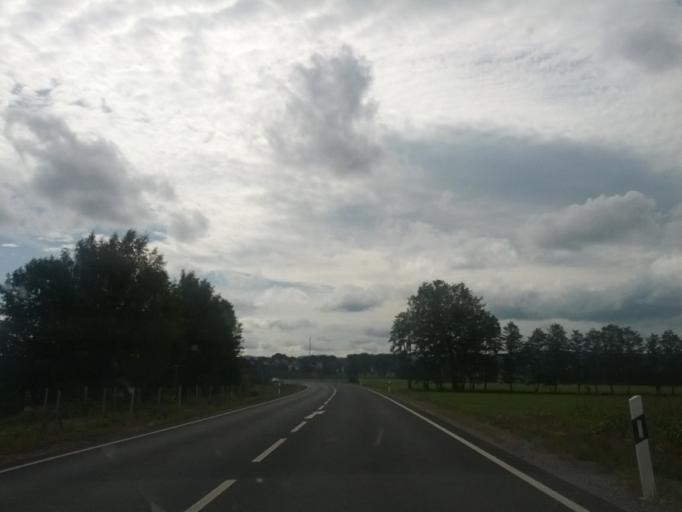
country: DE
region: Thuringia
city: Barchfeld
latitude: 50.8356
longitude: 10.2844
